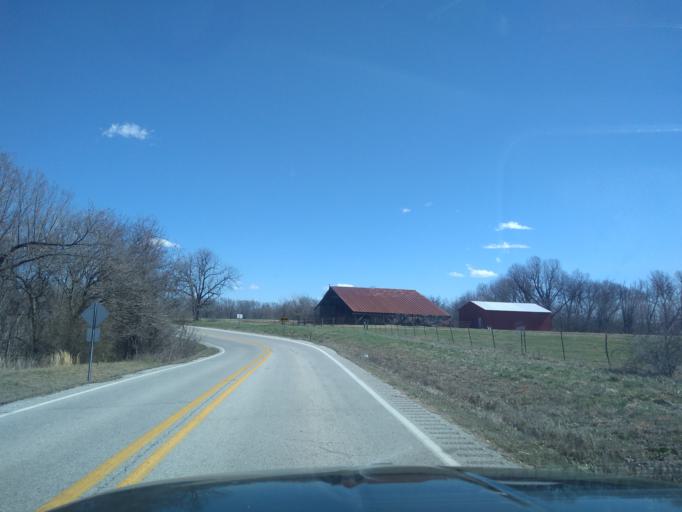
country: US
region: Arkansas
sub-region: Washington County
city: Farmington
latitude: 36.0797
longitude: -94.3069
